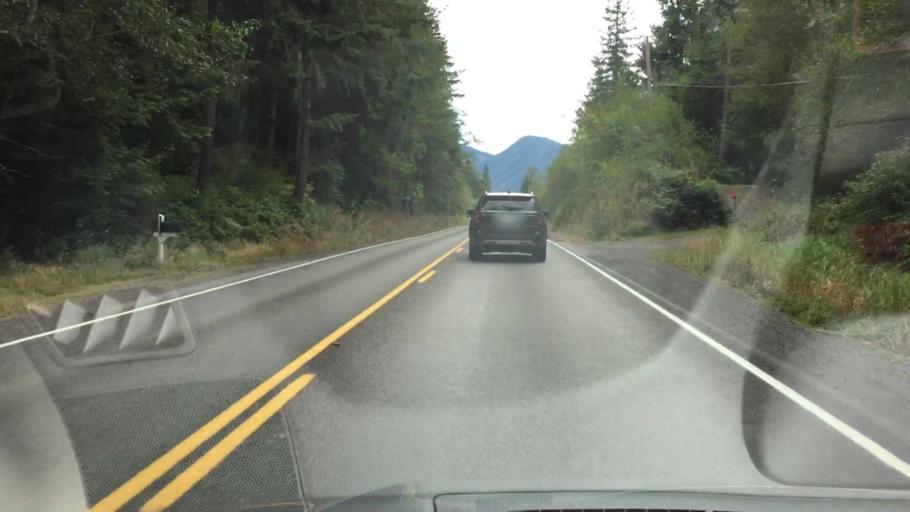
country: US
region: Washington
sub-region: Pierce County
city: Eatonville
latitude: 46.8154
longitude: -122.2664
